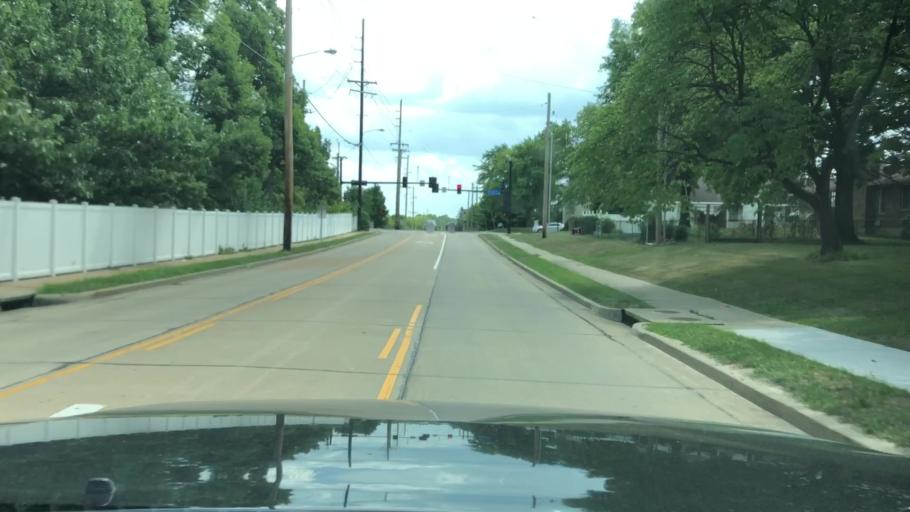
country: US
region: Missouri
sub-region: Saint Charles County
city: Saint Charles
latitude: 38.8041
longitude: -90.5355
